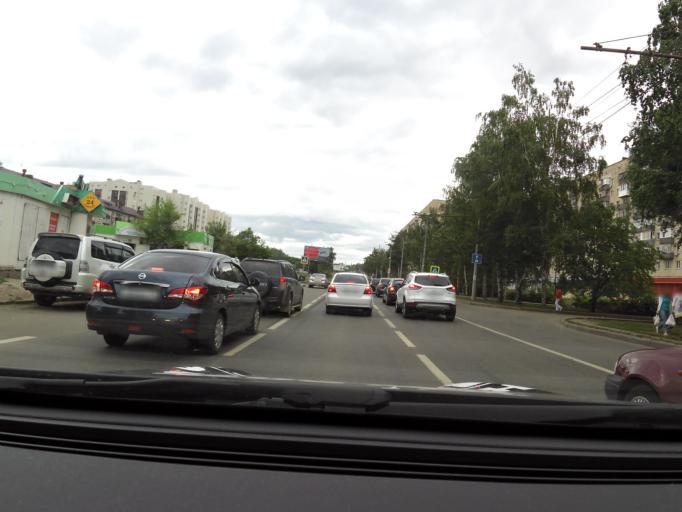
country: RU
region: Tatarstan
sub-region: Gorod Kazan'
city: Kazan
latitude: 55.8196
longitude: 49.0547
